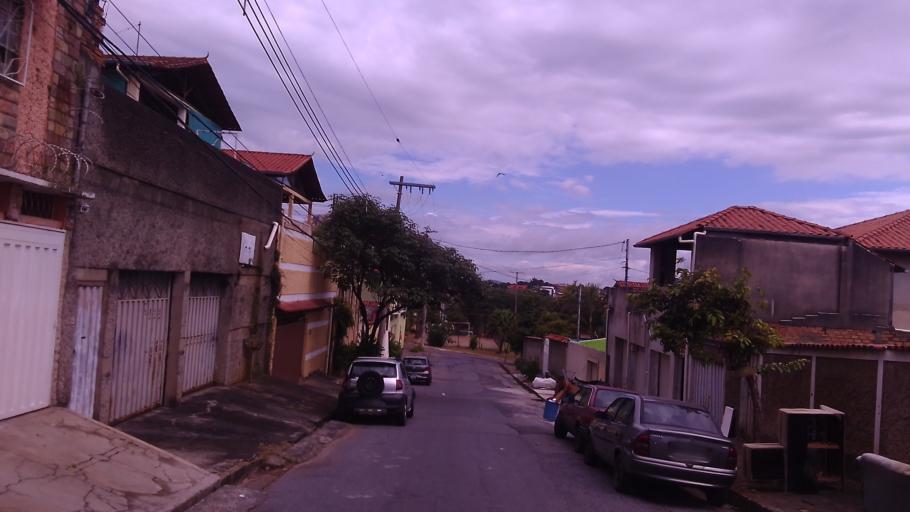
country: BR
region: Minas Gerais
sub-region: Contagem
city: Contagem
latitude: -19.9127
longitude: -44.0183
